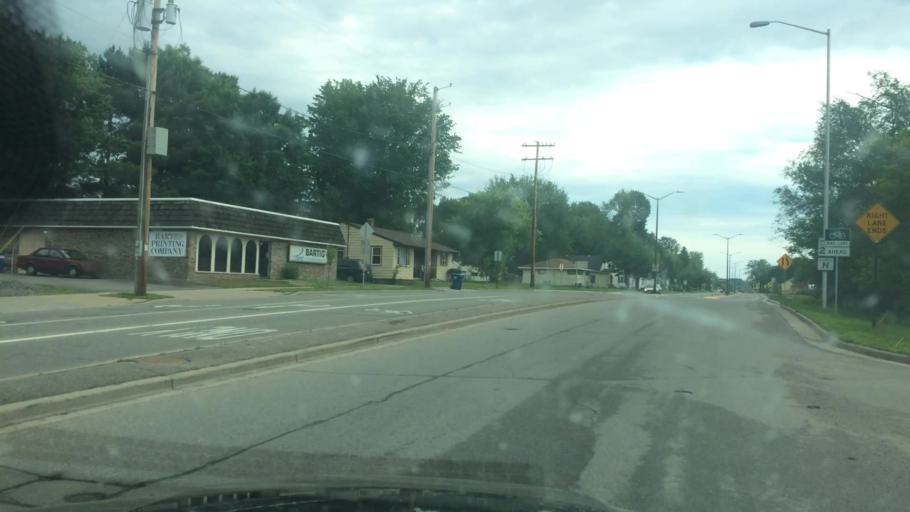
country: US
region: Wisconsin
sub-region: Marathon County
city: Wausau
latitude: 44.9483
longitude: -89.6550
